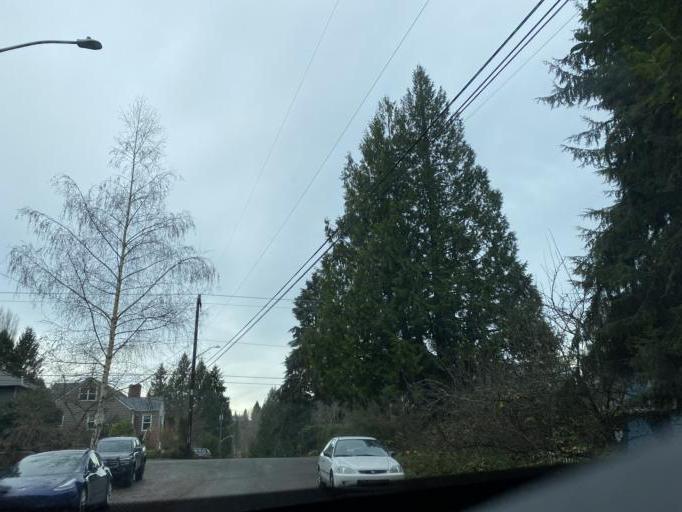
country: US
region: Washington
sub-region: King County
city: Lake Forest Park
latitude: 47.6966
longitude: -122.3009
